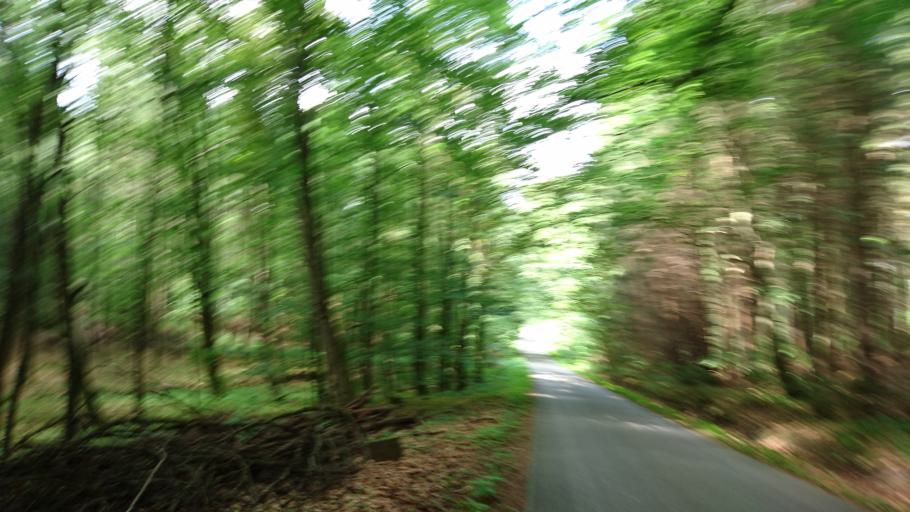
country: DE
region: Saxony
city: Bad Schandau
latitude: 50.8690
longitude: 14.1783
